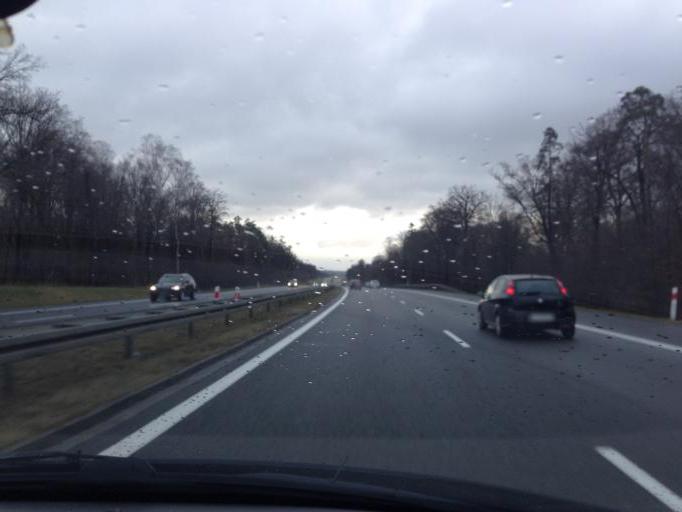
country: PL
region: Opole Voivodeship
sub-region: Powiat strzelecki
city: Ujazd
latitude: 50.4315
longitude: 18.3721
